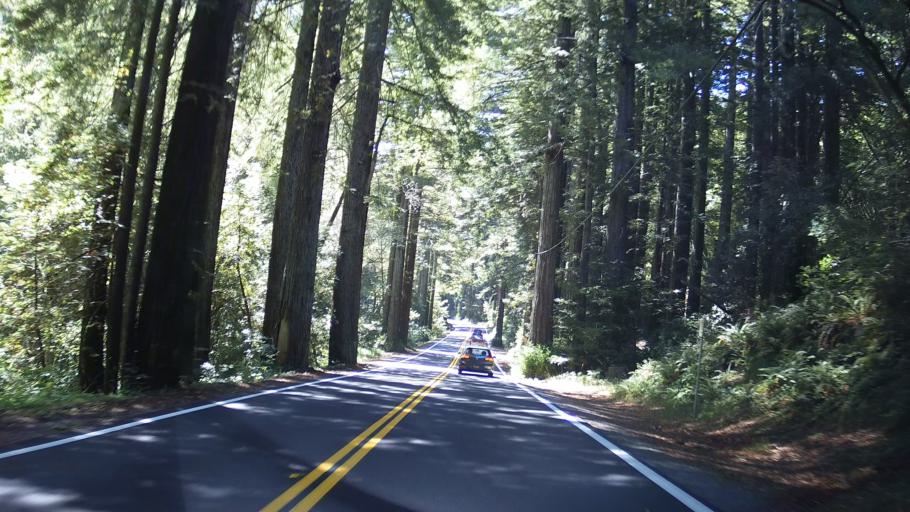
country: US
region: California
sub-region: Marin County
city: Lagunitas-Forest Knolls
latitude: 38.0195
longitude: -122.7249
